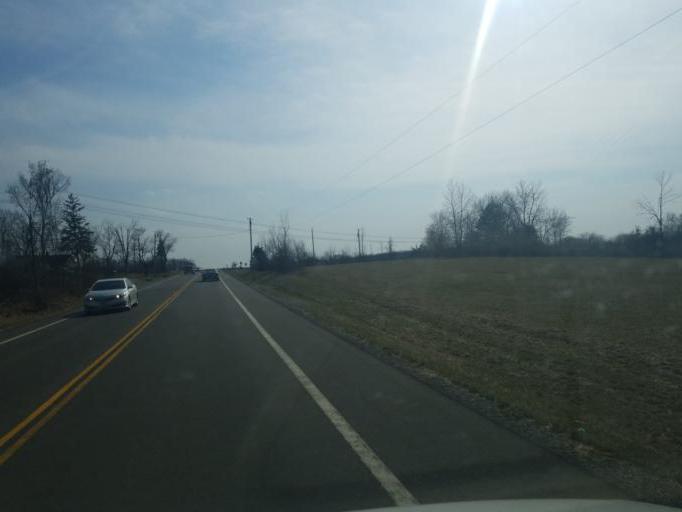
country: US
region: Ohio
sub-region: Logan County
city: Northwood
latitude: 40.4507
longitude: -83.7279
